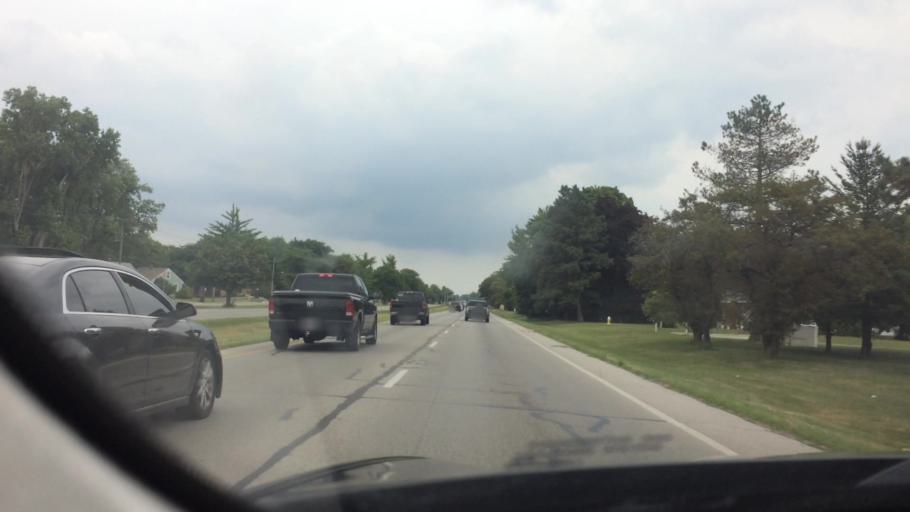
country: US
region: Ohio
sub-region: Lucas County
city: Maumee
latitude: 41.5741
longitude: -83.6382
